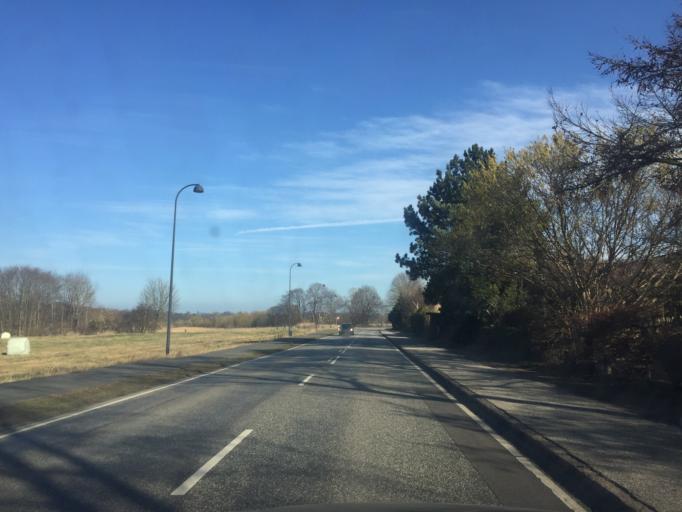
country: DK
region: Capital Region
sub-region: Rudersdal Kommune
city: Trorod
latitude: 55.8489
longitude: 12.5433
